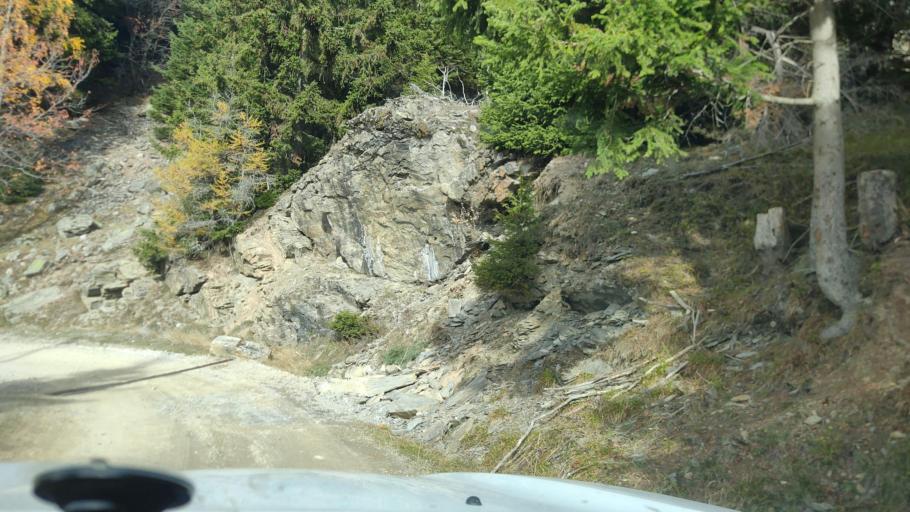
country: FR
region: Rhone-Alpes
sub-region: Departement de la Savoie
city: Modane
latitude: 45.2027
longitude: 6.6459
